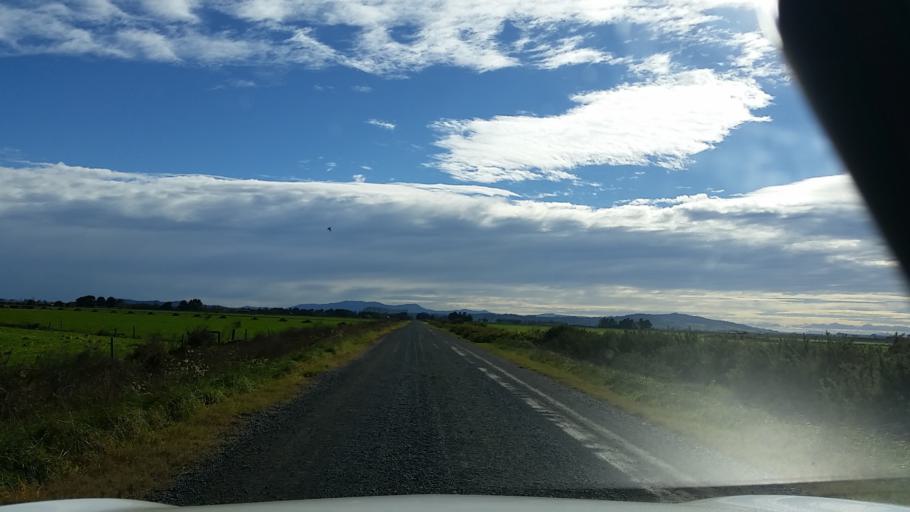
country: NZ
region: Waikato
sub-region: Hamilton City
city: Hamilton
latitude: -37.6830
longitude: 175.4441
